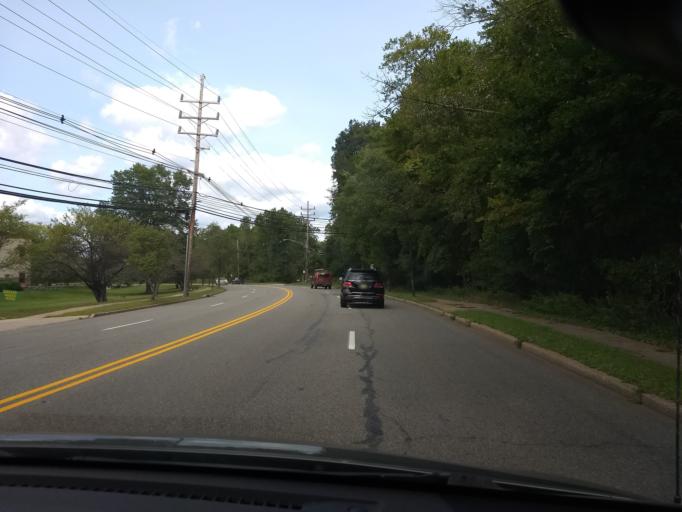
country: US
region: New Jersey
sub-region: Morris County
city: Parsippany
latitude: 40.8300
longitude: -74.4453
